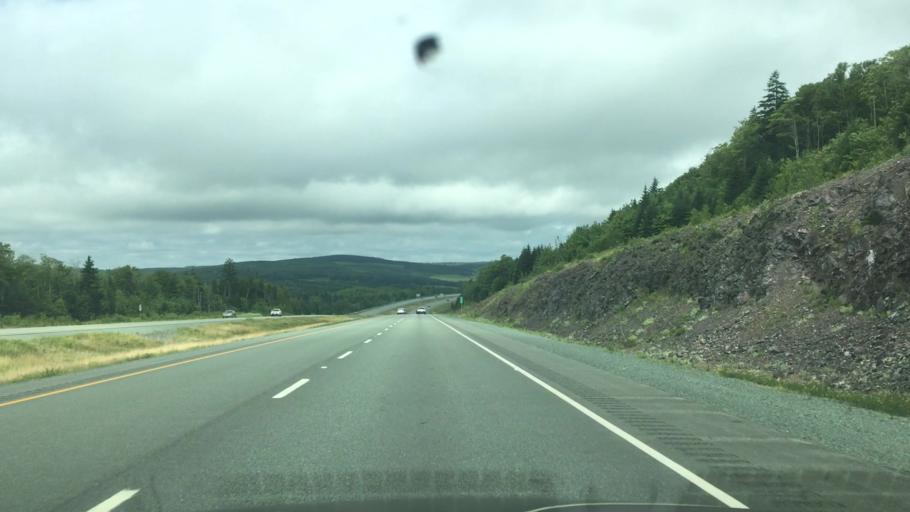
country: CA
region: Nova Scotia
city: Oxford
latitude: 45.5239
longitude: -63.7044
